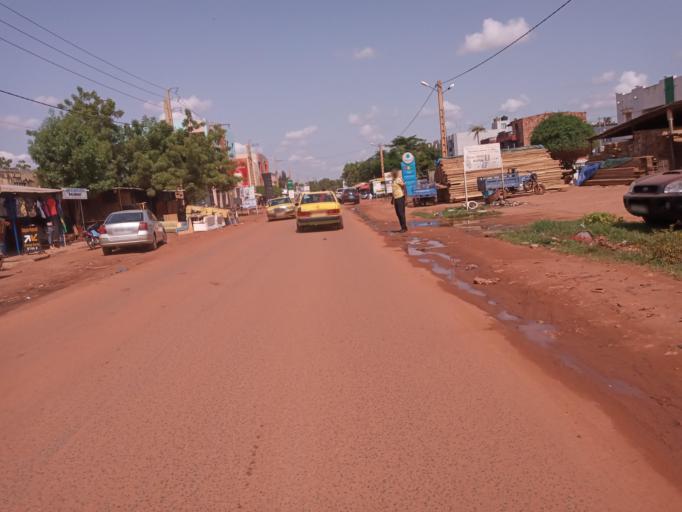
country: ML
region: Bamako
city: Bamako
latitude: 12.5966
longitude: -8.0191
